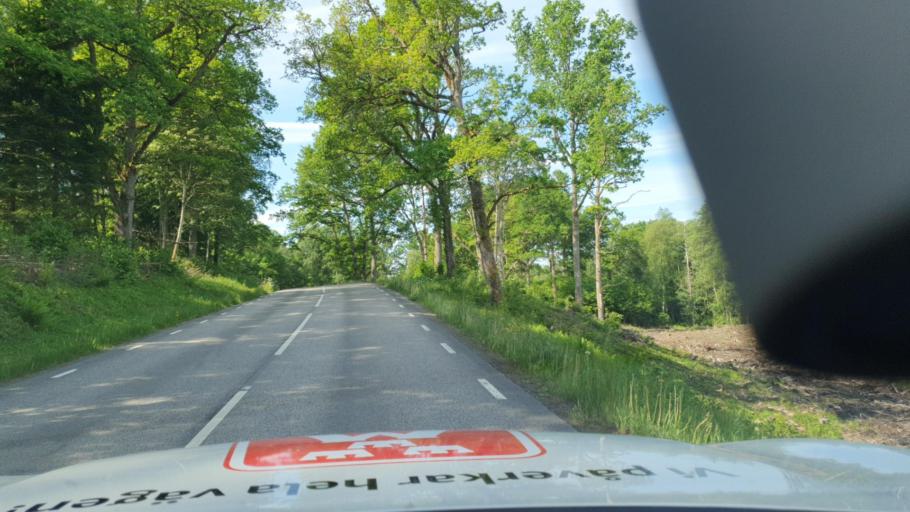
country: SE
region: Vaestra Goetaland
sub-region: Falkopings Kommun
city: Floby
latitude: 58.1130
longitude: 13.2853
